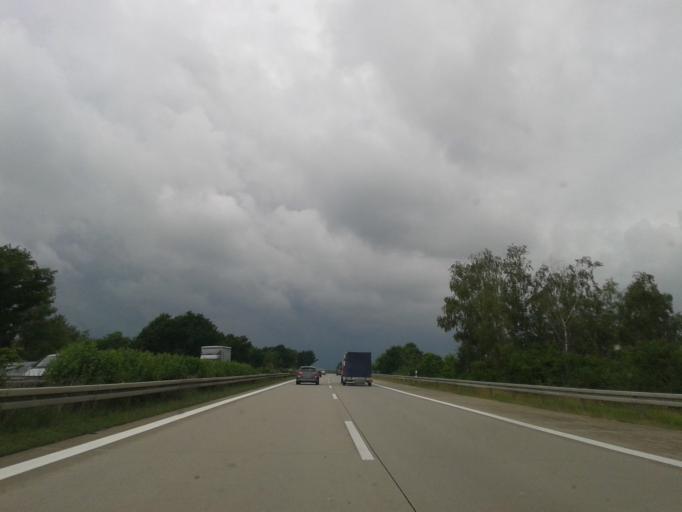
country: DE
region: Saxony
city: Mochau
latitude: 51.1056
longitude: 13.1924
